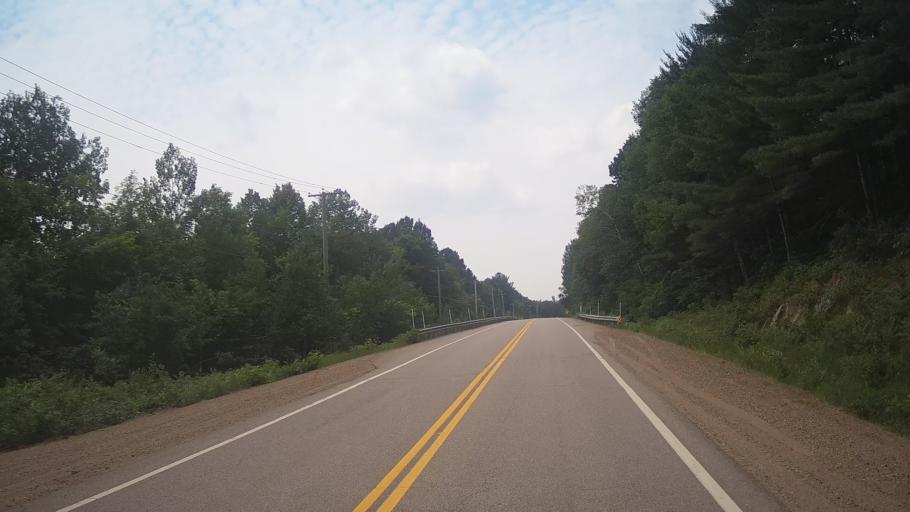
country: CA
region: Ontario
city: Pembroke
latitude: 45.9158
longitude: -76.9506
